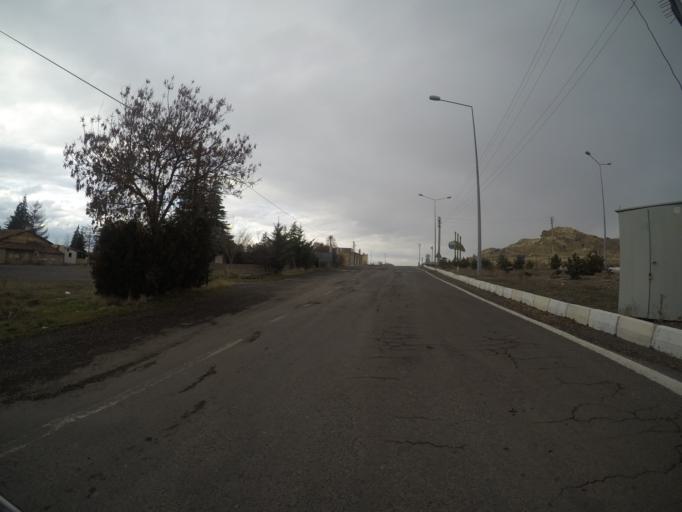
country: TR
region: Nevsehir
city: Goereme
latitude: 38.6316
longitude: 34.8574
